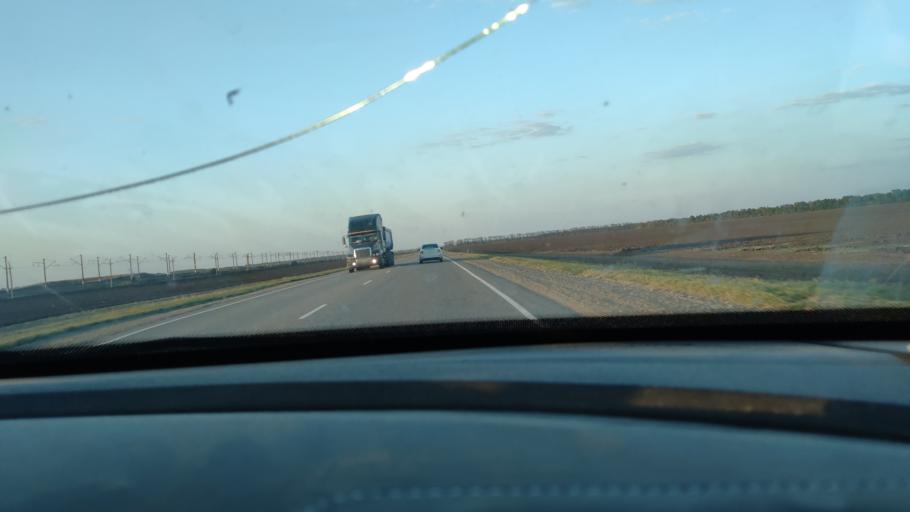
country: RU
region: Krasnodarskiy
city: Novominskaya
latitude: 46.3354
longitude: 38.9476
